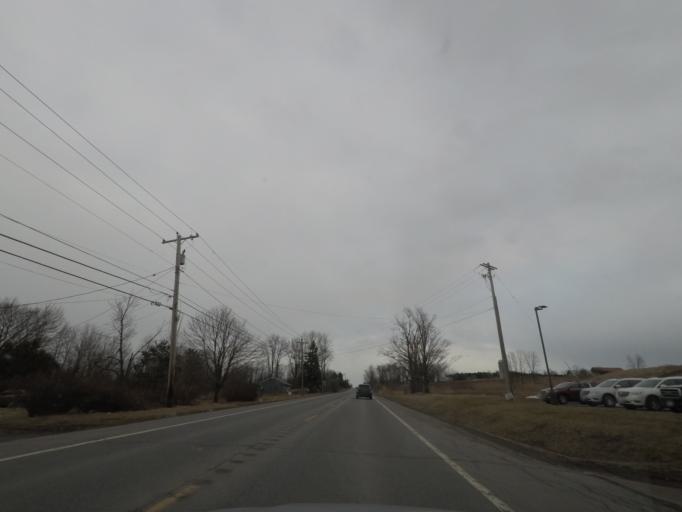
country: US
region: New York
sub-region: Madison County
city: Wampsville
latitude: 43.0767
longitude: -75.6820
